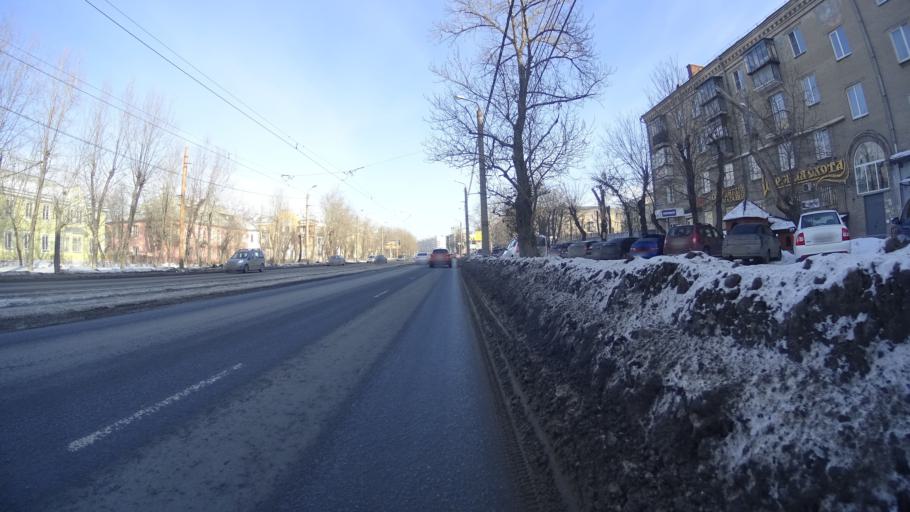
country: RU
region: Chelyabinsk
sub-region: Gorod Chelyabinsk
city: Chelyabinsk
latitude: 55.1856
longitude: 61.4264
